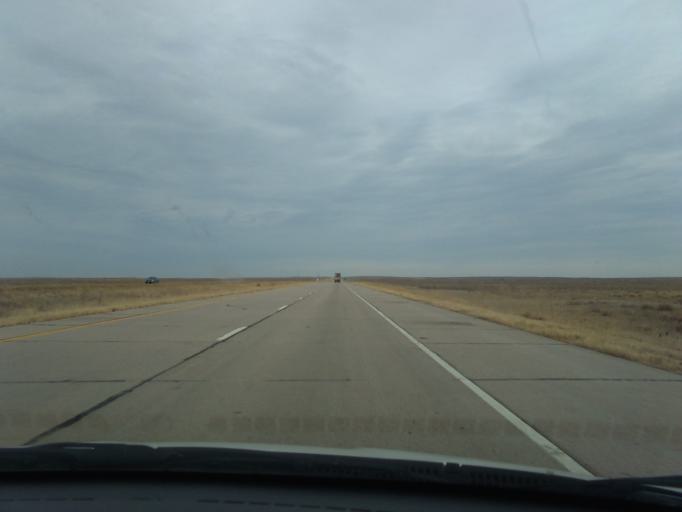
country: US
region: Colorado
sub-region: Weld County
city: Keenesburg
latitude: 40.2056
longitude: -104.2439
